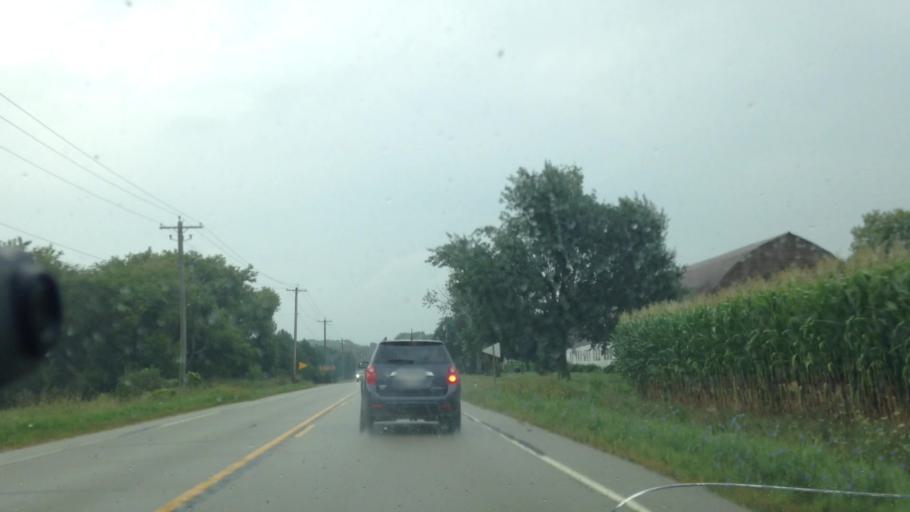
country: US
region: Wisconsin
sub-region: Washington County
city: Hartford
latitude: 43.3882
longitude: -88.3558
